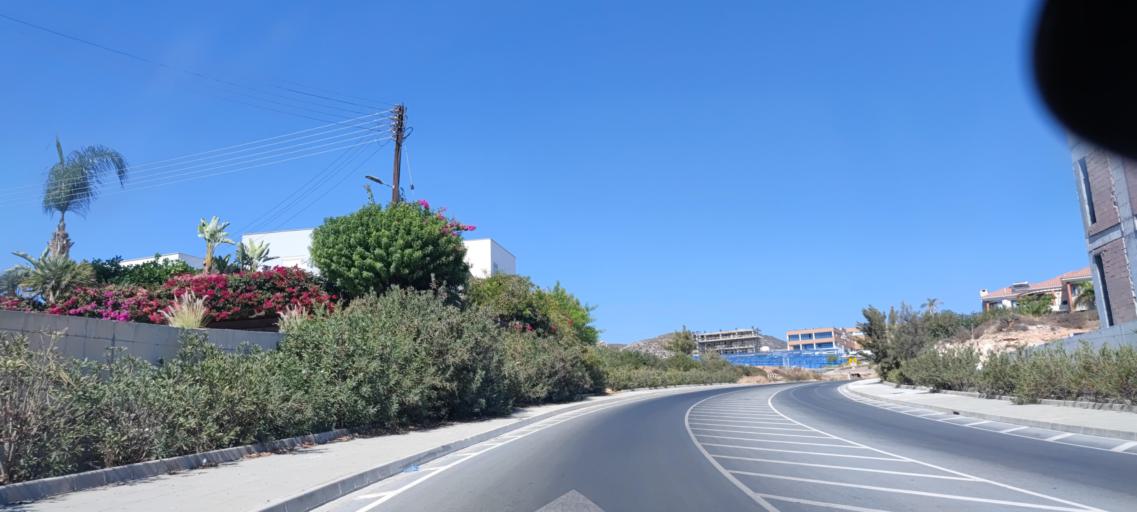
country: CY
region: Limassol
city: Mouttagiaka
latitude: 34.7261
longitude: 33.0615
